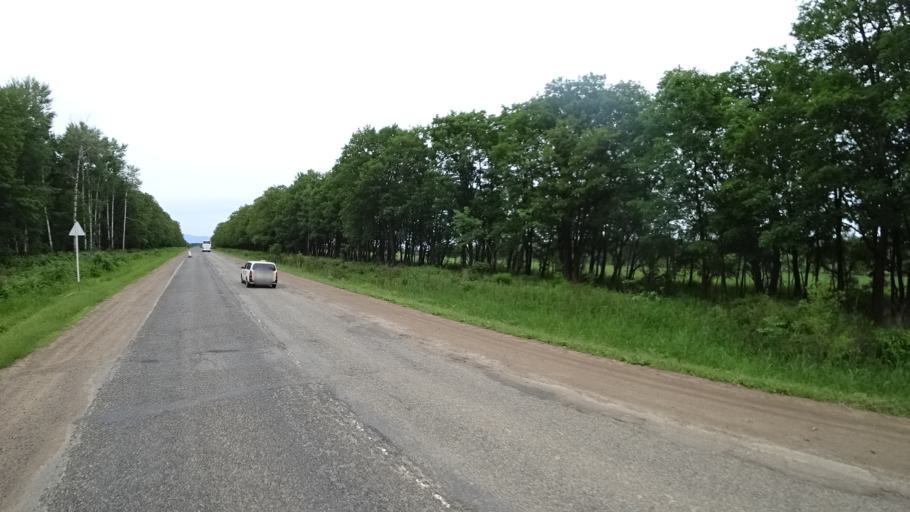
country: RU
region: Primorskiy
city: Novosysoyevka
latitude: 44.1925
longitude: 133.3539
